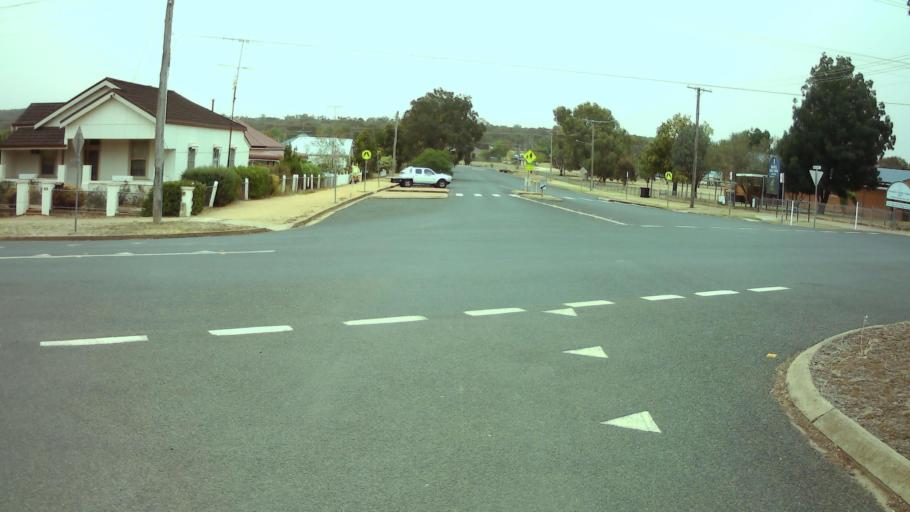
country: AU
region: New South Wales
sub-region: Weddin
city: Grenfell
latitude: -33.8932
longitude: 148.1660
